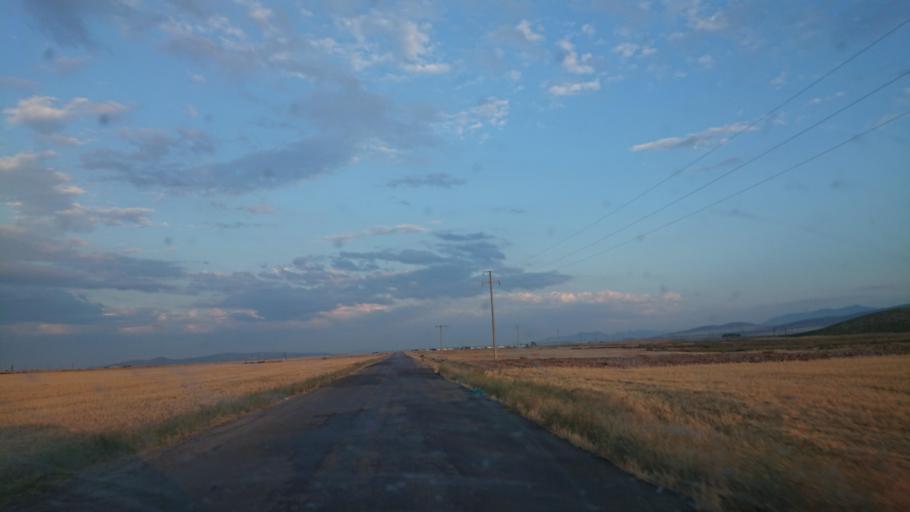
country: TR
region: Aksaray
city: Agacoren
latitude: 38.8927
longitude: 34.0518
